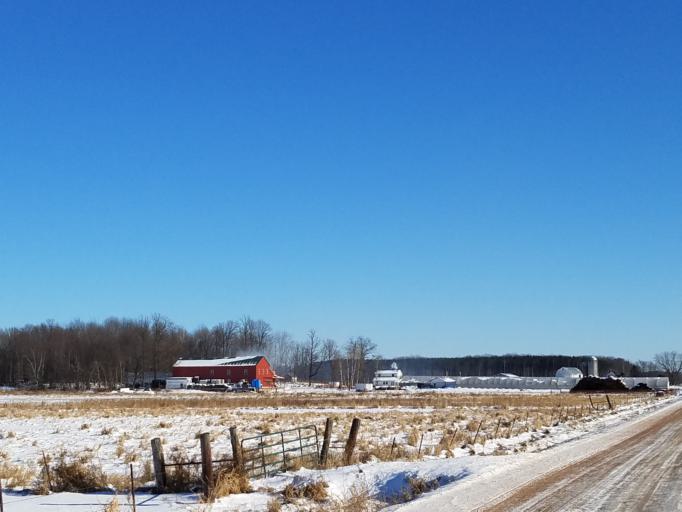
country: US
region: Wisconsin
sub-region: Clark County
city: Neillsville
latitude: 44.5538
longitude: -90.3918
